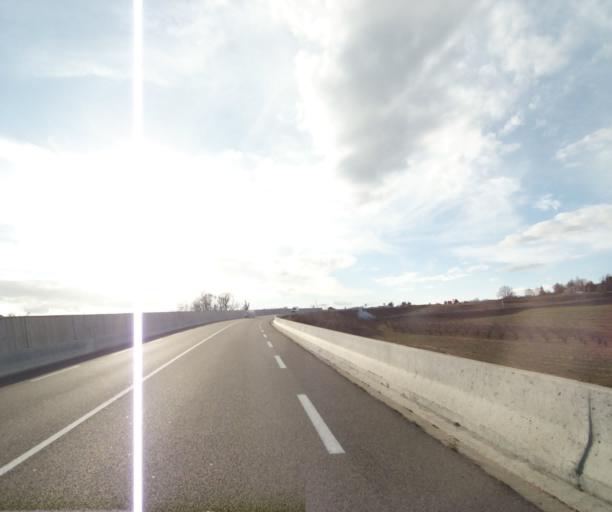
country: FR
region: Rhone-Alpes
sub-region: Departement de l'Ardeche
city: Davezieux
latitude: 45.2619
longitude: 4.7112
